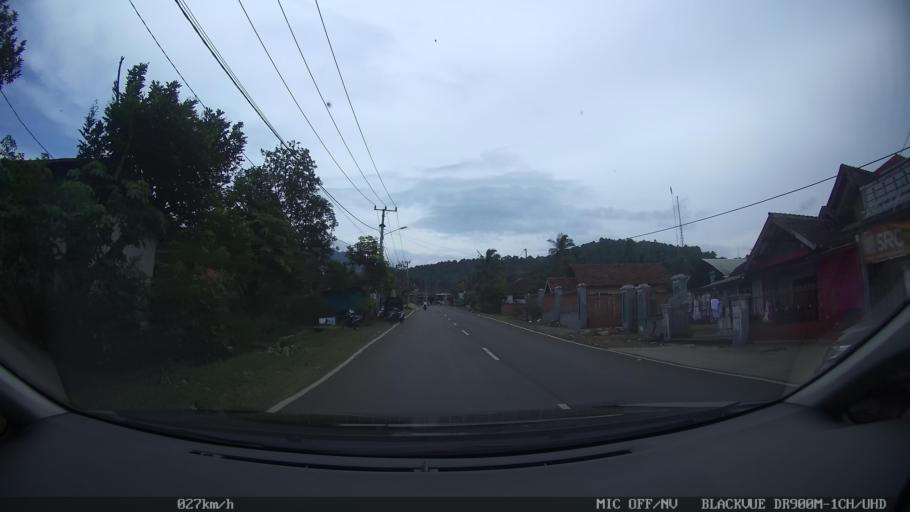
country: ID
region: Lampung
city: Bandarlampung
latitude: -5.4159
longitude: 105.1880
